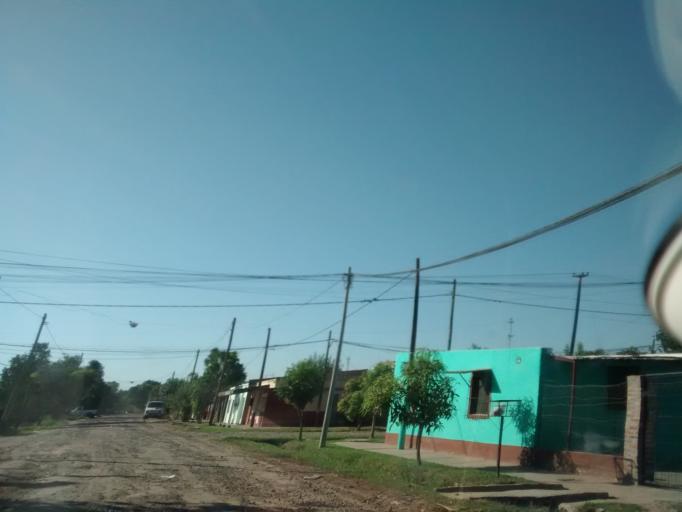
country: AR
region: Chaco
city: Fontana
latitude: -27.4409
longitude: -59.0103
